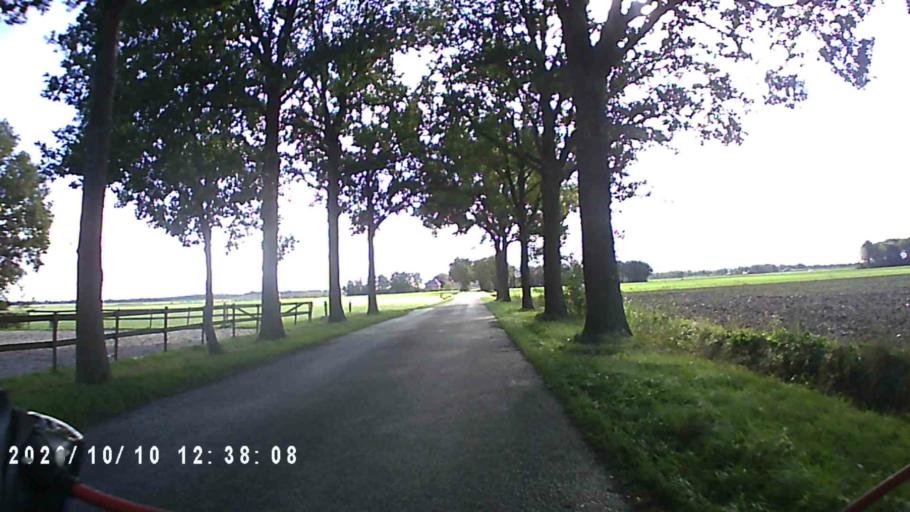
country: NL
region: Friesland
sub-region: Gemeente Weststellingwerf
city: Noordwolde
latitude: 52.9492
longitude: 6.2038
